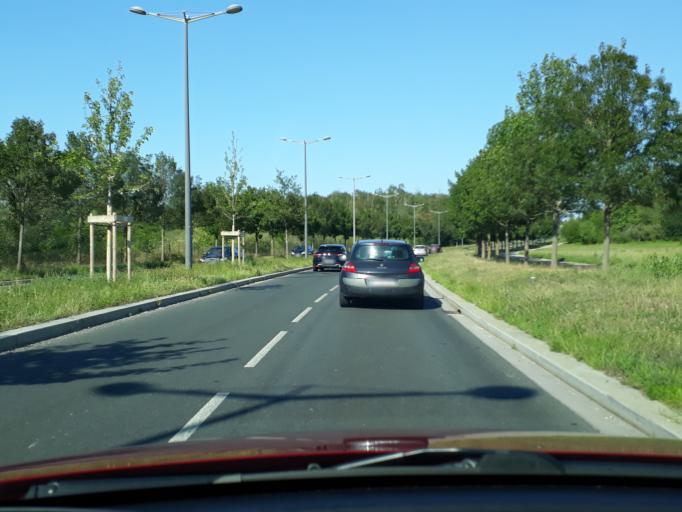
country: FR
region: Rhone-Alpes
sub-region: Departement du Rhone
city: Bron
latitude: 45.7125
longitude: 4.9211
